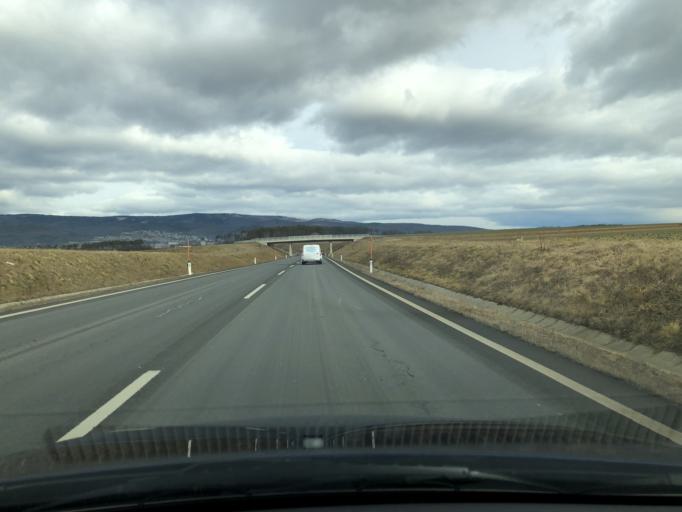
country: AT
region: Burgenland
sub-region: Politischer Bezirk Oberwart
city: Schachendorf
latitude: 47.2665
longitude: 16.4481
